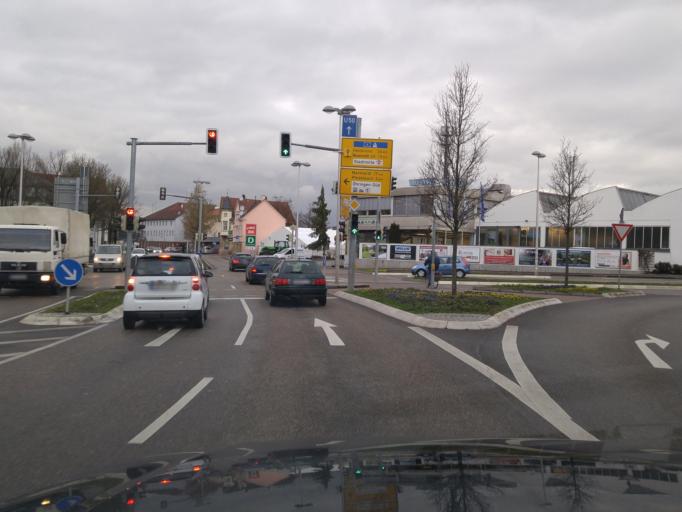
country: DE
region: Baden-Wuerttemberg
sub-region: Regierungsbezirk Stuttgart
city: Ohringen
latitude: 49.2015
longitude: 9.5064
